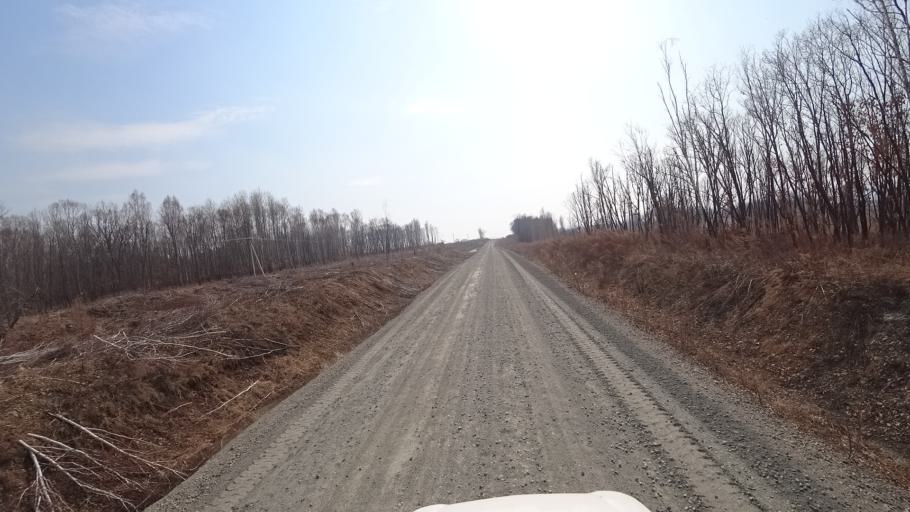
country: RU
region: Amur
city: Novobureyskiy
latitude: 49.8214
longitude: 129.9828
